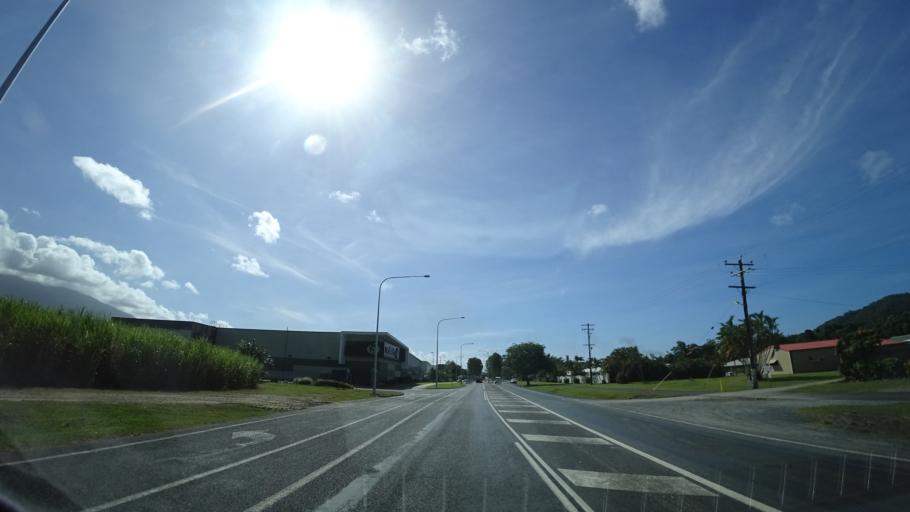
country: AU
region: Queensland
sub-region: Cairns
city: Port Douglas
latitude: -16.4676
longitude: 145.3729
